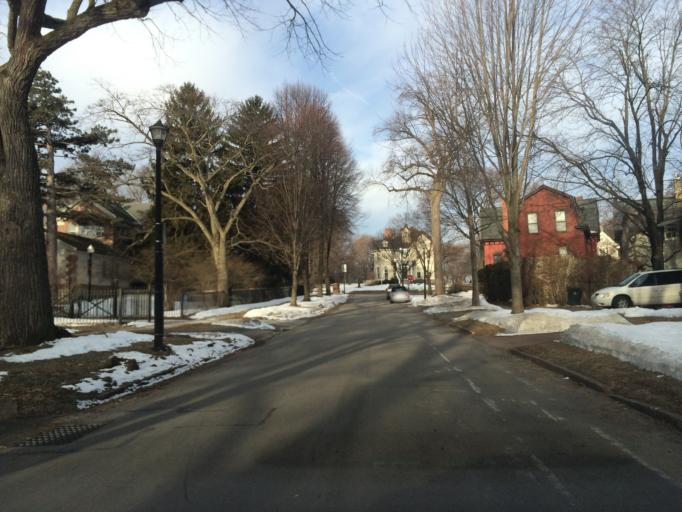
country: US
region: New York
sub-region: Monroe County
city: Rochester
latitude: 43.1387
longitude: -77.6132
